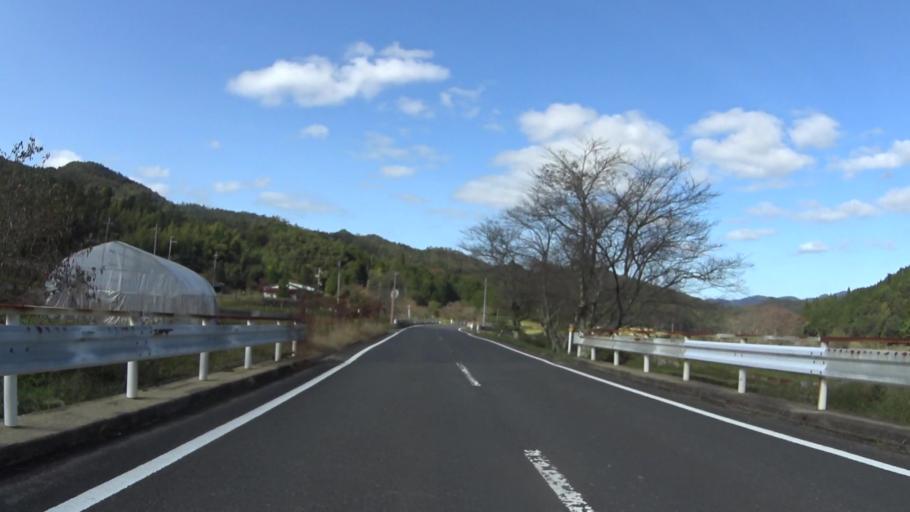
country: JP
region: Hyogo
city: Toyooka
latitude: 35.5483
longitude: 134.9786
